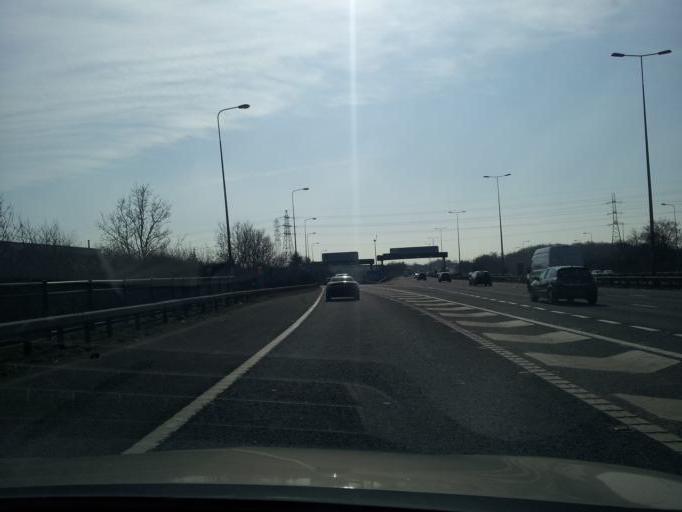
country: GB
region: England
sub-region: Leicestershire
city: Enderby
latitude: 52.6047
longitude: -1.1958
